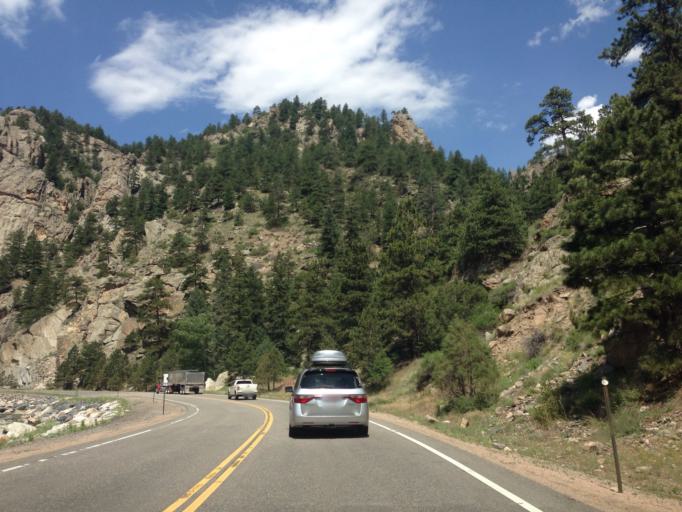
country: US
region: Colorado
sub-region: Larimer County
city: Estes Park
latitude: 40.4164
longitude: -105.3708
